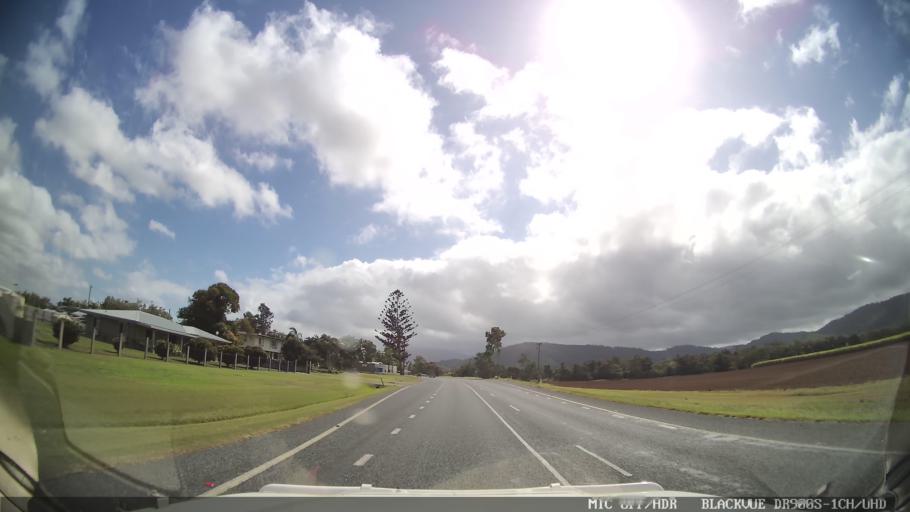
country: AU
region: Queensland
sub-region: Whitsunday
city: Proserpine
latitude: -20.3530
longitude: 148.5562
